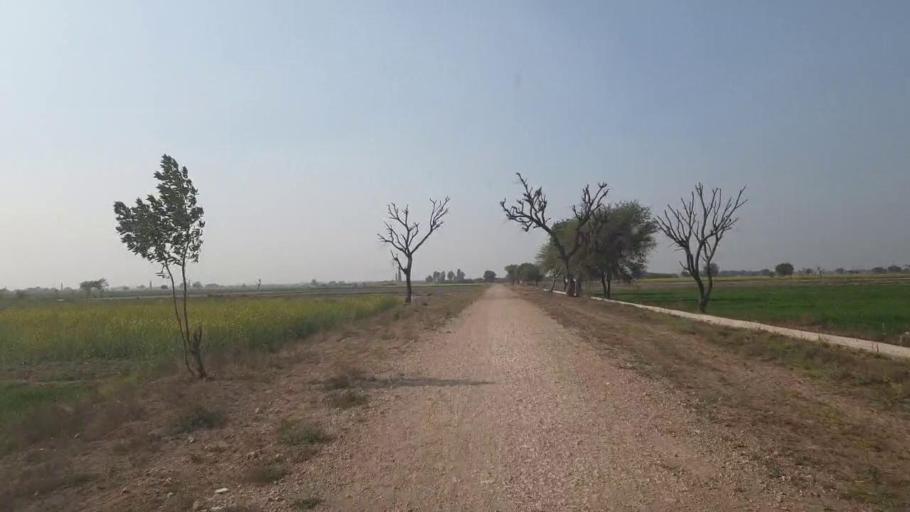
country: PK
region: Sindh
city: Tando Allahyar
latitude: 25.4393
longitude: 68.7058
